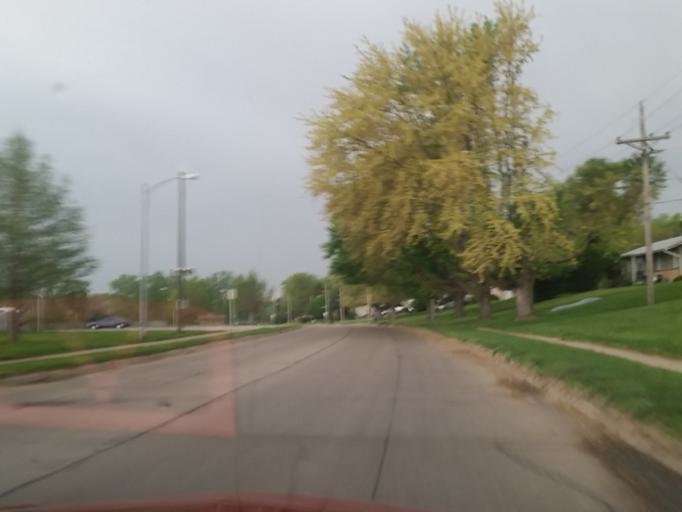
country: US
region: Nebraska
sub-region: Sarpy County
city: Offutt Air Force Base
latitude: 41.1460
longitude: -95.9207
